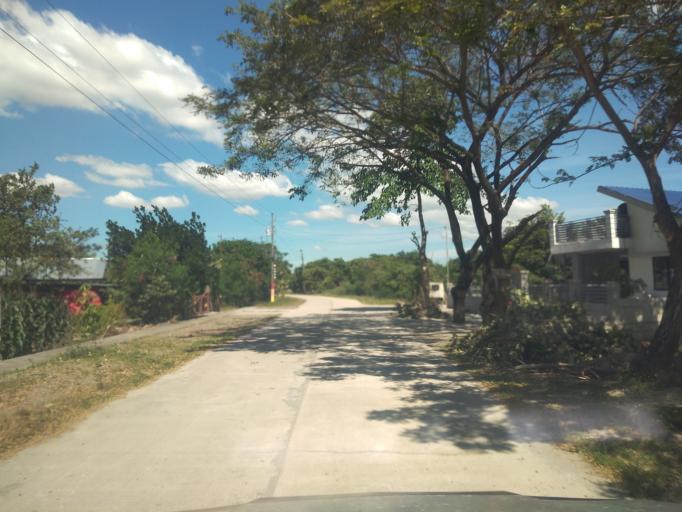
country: PH
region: Central Luzon
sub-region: Province of Pampanga
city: San Basilio
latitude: 15.0318
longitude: 120.6062
